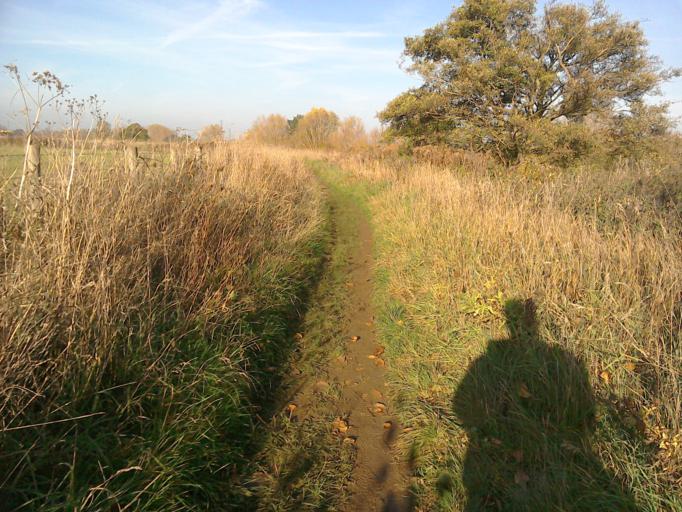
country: GB
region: England
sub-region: Oxfordshire
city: Radley
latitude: 51.6870
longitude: -1.2222
